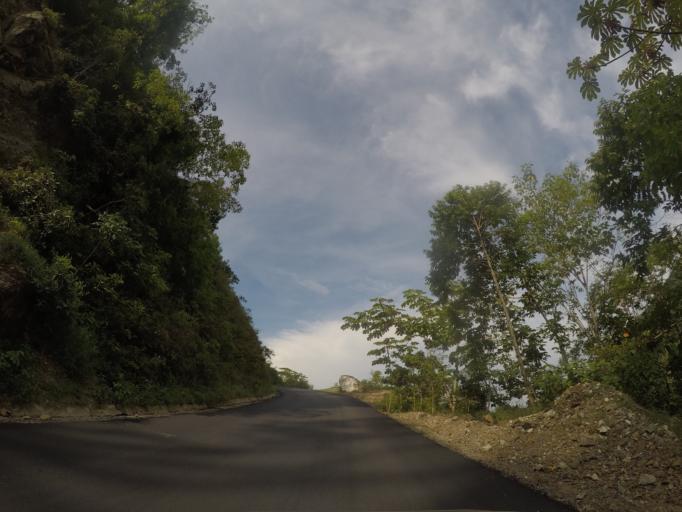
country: MX
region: Oaxaca
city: Pluma Hidalgo
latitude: 15.9382
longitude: -96.4312
